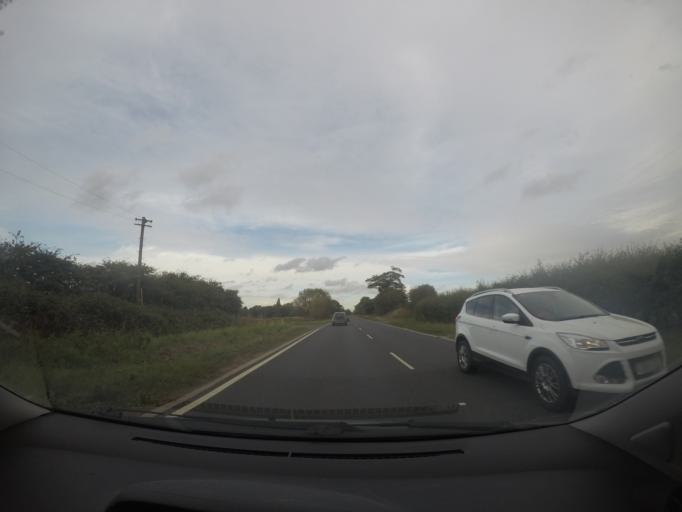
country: GB
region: England
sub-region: City of York
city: Deighton
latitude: 53.8989
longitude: -1.0478
